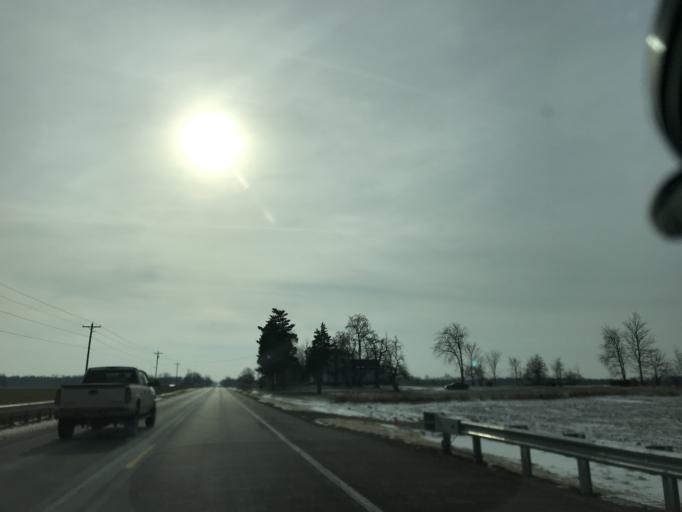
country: US
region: Michigan
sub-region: Ionia County
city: Lake Odessa
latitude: 42.8240
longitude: -85.0748
